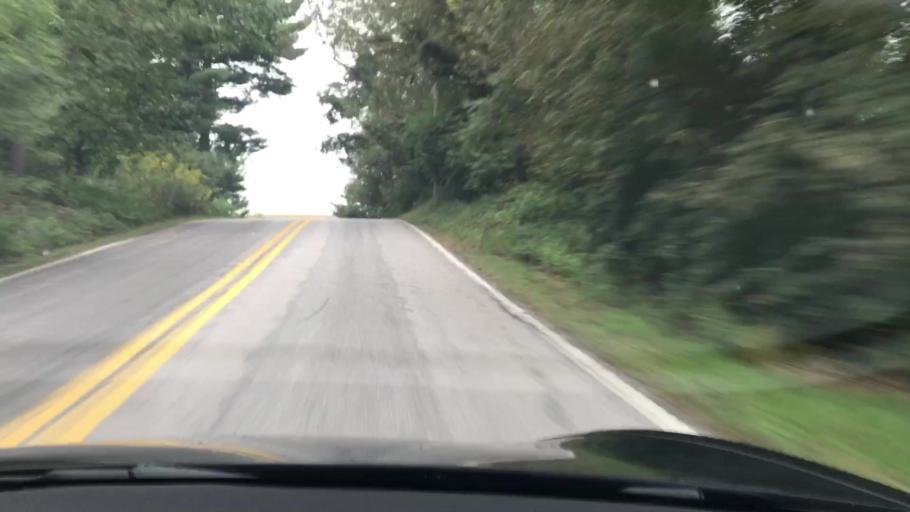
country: US
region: Pennsylvania
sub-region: York County
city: Weigelstown
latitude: 39.9509
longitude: -76.8601
